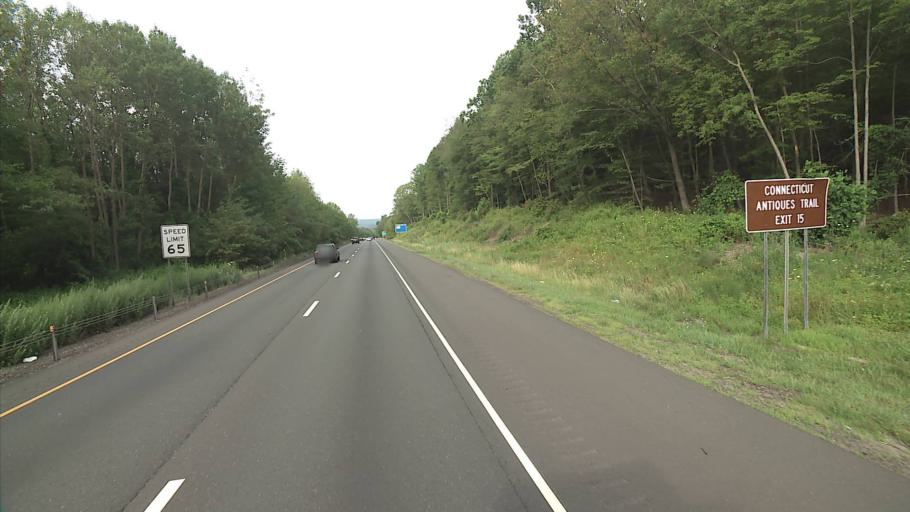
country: US
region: Connecticut
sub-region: New Haven County
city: Southbury
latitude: 41.4857
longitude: -73.1845
